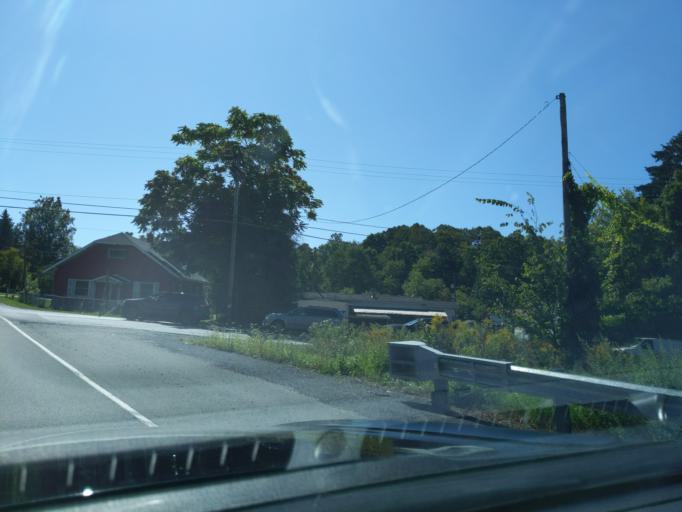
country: US
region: Pennsylvania
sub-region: Blair County
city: Greenwood
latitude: 40.5282
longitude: -78.3639
